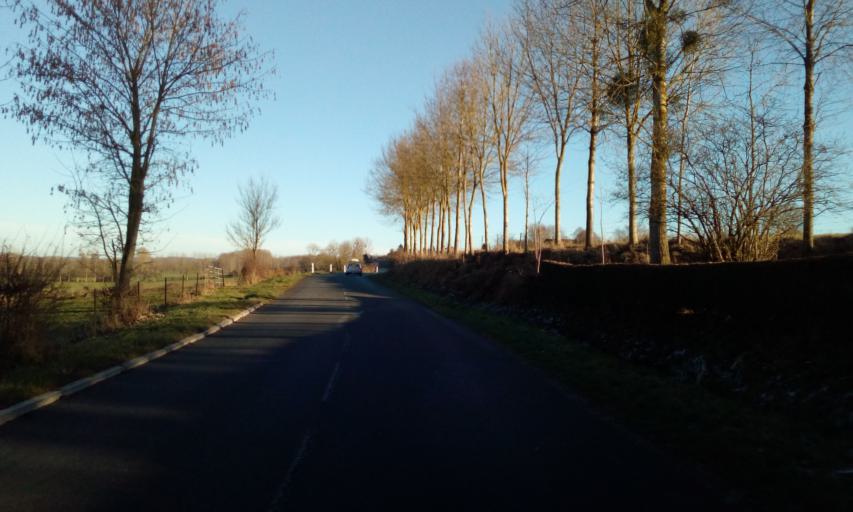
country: FR
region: Picardie
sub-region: Departement de l'Aisne
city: Rozoy-sur-Serre
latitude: 49.7079
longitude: 4.1427
